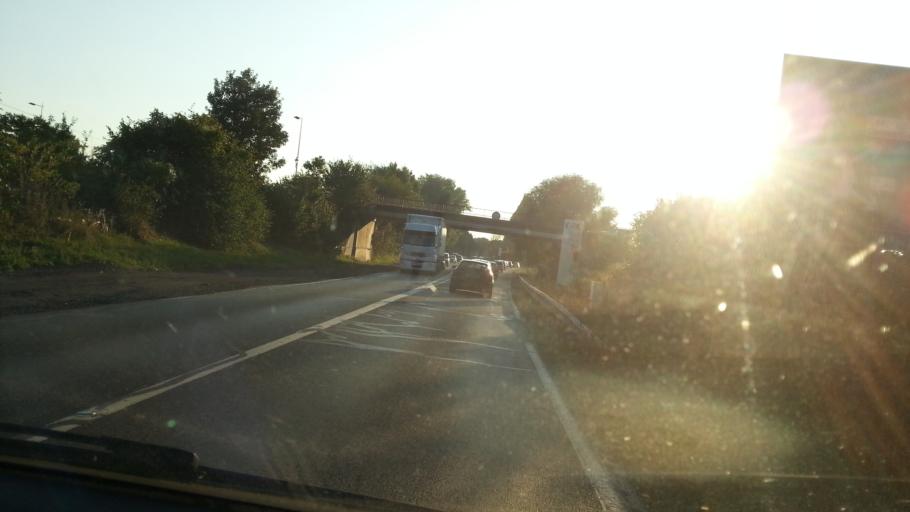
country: FR
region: Picardie
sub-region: Departement de l'Oise
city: Villers-Saint-Paul
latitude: 49.2895
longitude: 2.5020
